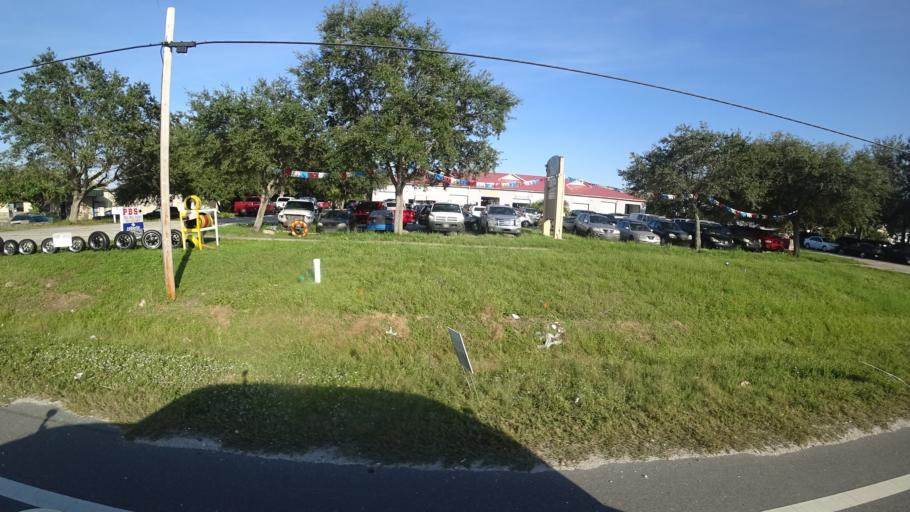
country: US
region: Florida
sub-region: Manatee County
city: Samoset
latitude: 27.4379
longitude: -82.5466
